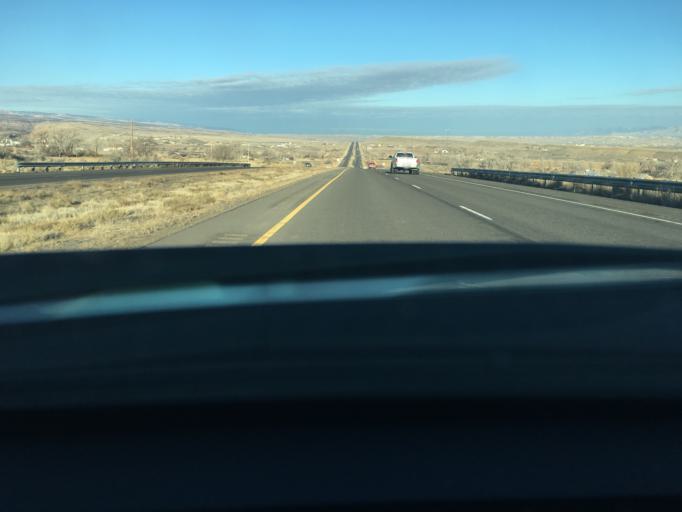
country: US
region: Colorado
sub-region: Mesa County
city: Clifton
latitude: 38.9268
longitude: -108.3856
